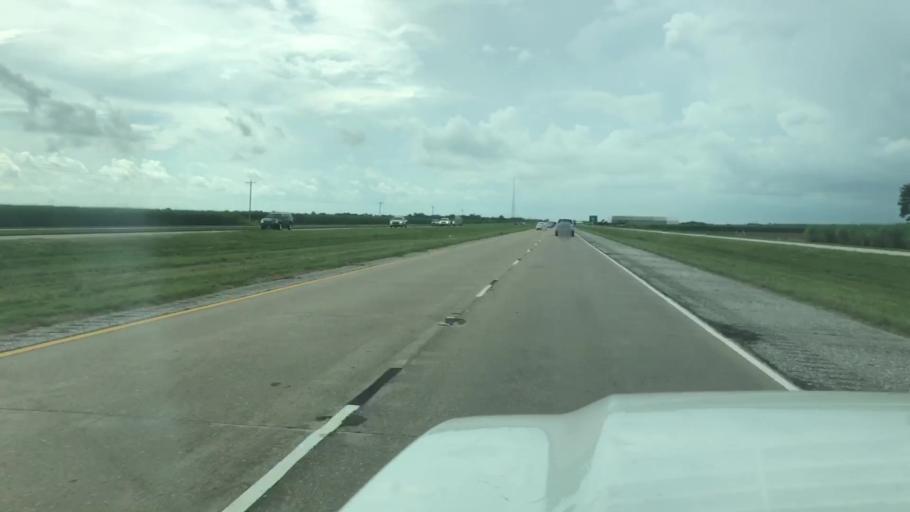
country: US
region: Louisiana
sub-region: Iberia Parish
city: Jeanerette
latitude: 29.9061
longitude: -91.7078
